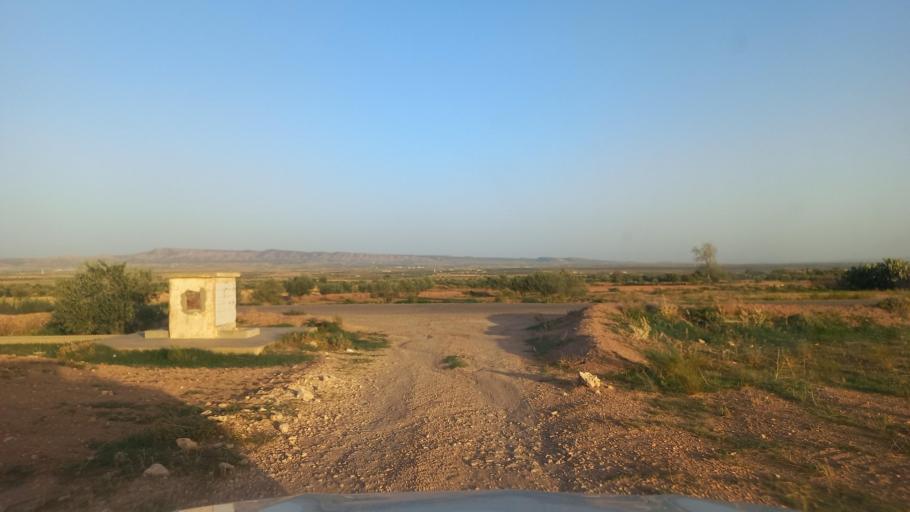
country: TN
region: Al Qasrayn
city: Sbiba
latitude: 35.3717
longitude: 9.0120
